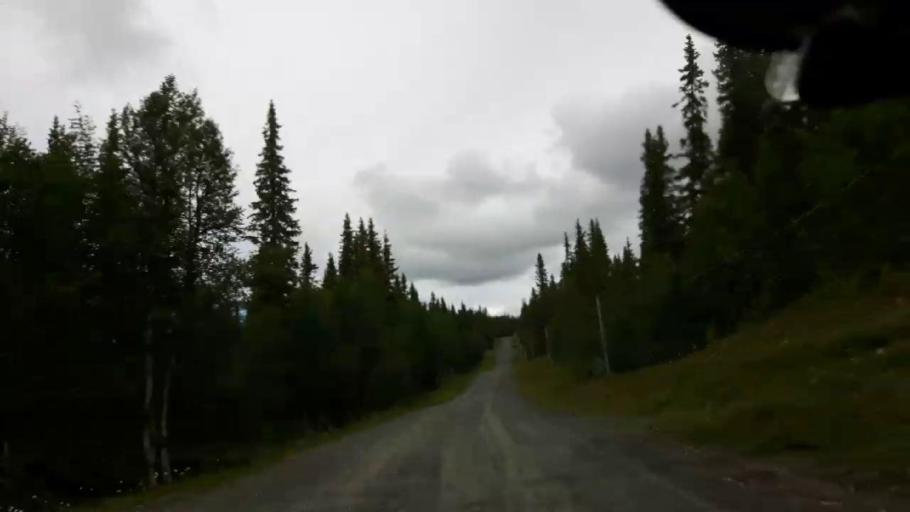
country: SE
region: Jaemtland
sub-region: Krokoms Kommun
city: Valla
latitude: 63.7471
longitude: 13.8354
